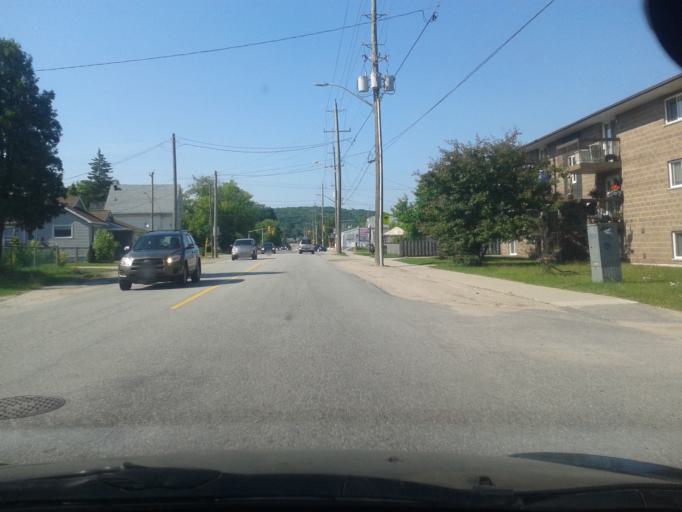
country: CA
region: Ontario
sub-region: Nipissing District
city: North Bay
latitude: 46.3264
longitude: -79.4572
